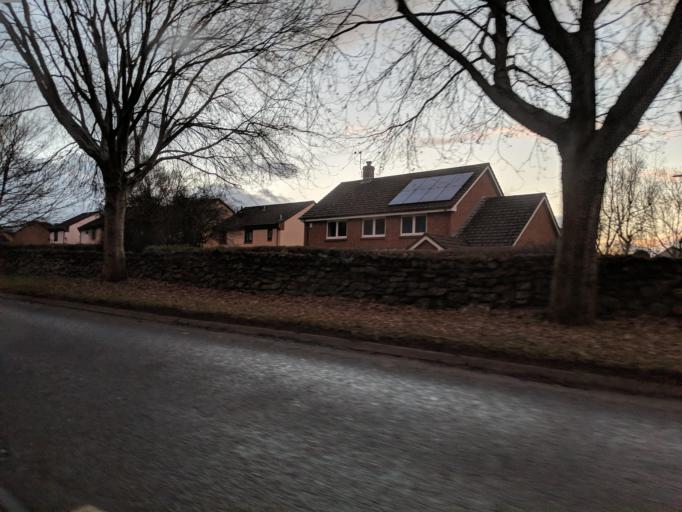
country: GB
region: England
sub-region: Devon
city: Barnstaple
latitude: 51.0688
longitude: -4.0859
